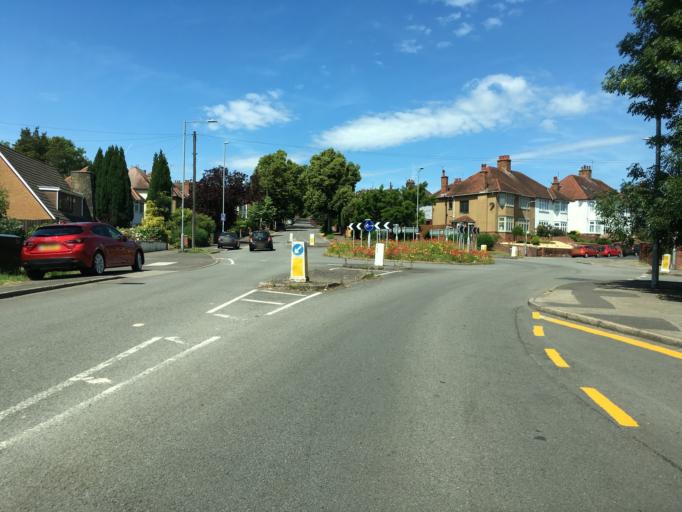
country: GB
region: Wales
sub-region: Newport
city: Newport
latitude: 51.5905
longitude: -3.0071
